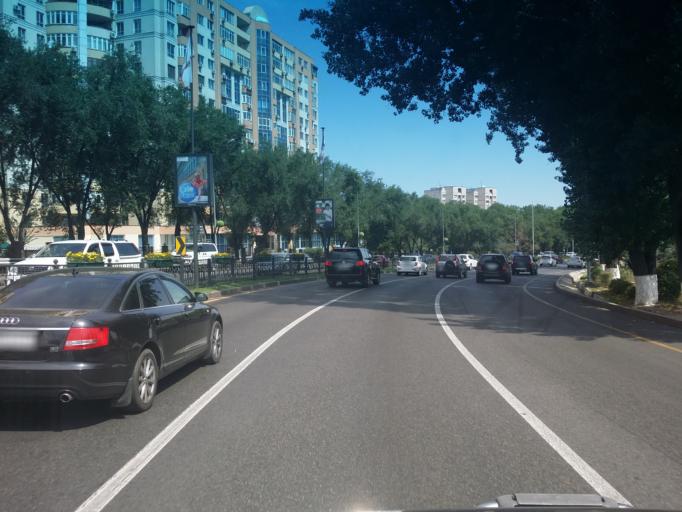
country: KZ
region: Almaty Qalasy
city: Almaty
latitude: 43.2072
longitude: 76.9138
